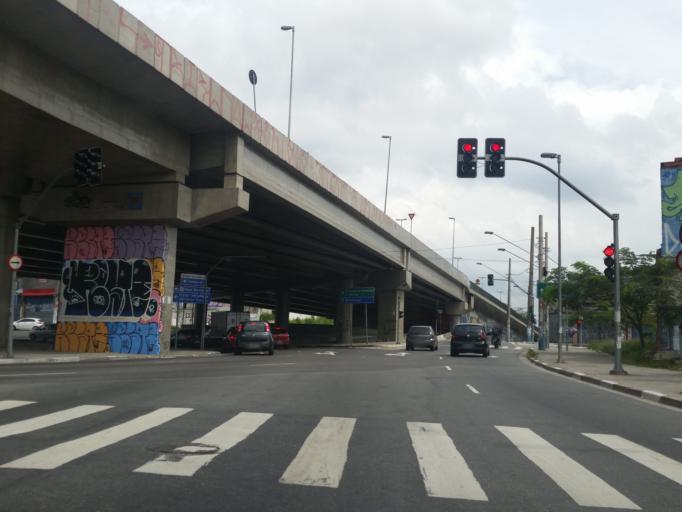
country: BR
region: Sao Paulo
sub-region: Ferraz De Vasconcelos
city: Ferraz de Vasconcelos
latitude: -23.5349
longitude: -46.4544
